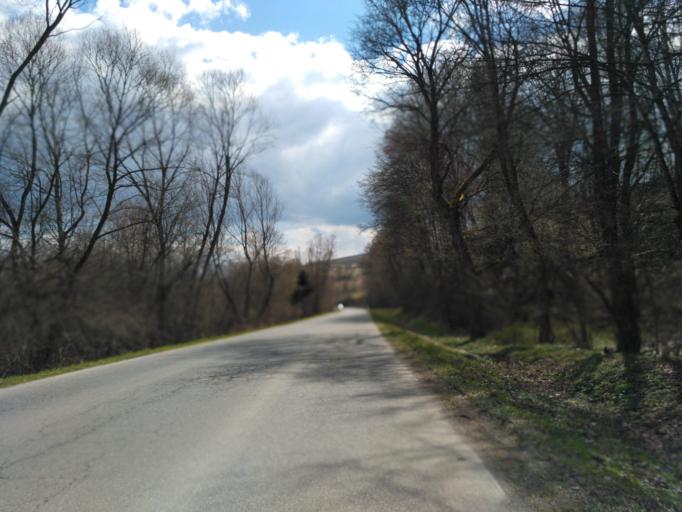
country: PL
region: Subcarpathian Voivodeship
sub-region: Powiat sanocki
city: Tyrawa Woloska
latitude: 49.5846
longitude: 22.3452
